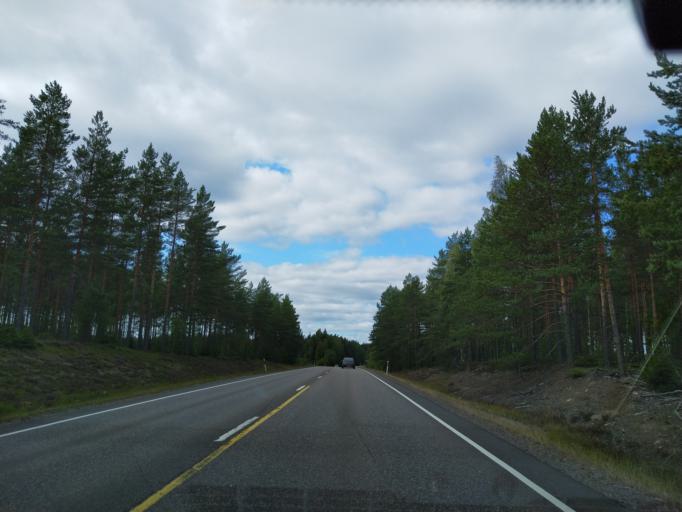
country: FI
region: Haeme
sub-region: Riihimaeki
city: Loppi
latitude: 60.7484
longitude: 24.3306
